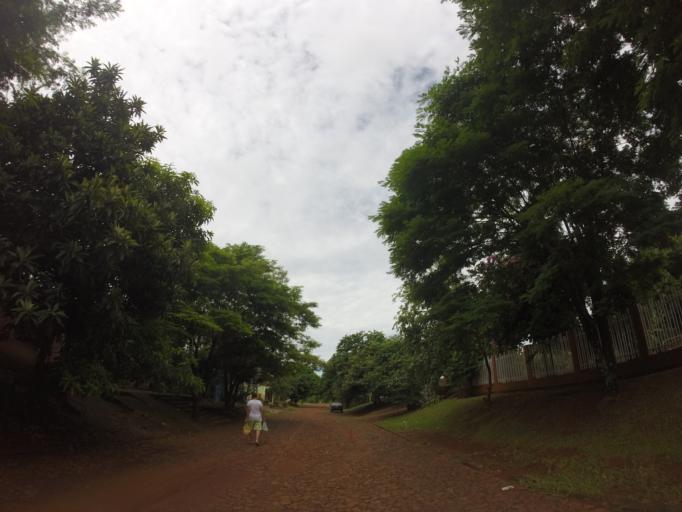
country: PY
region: Alto Parana
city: Ciudad del Este
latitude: -25.4073
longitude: -54.6484
